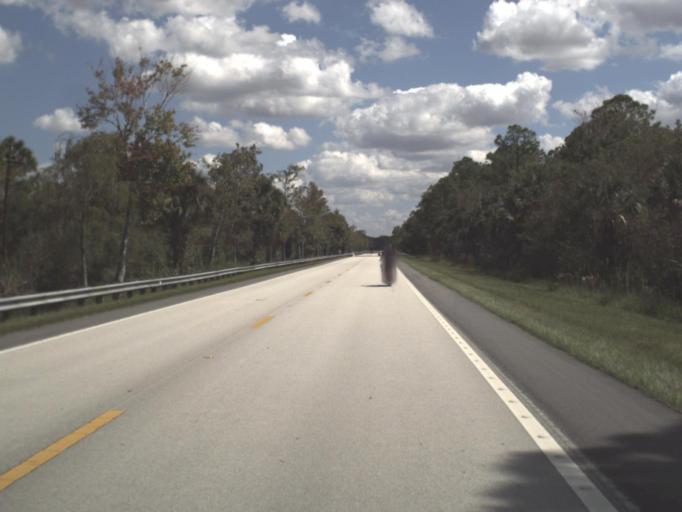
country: US
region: Florida
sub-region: Collier County
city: Marco
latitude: 25.8822
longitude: -81.2498
